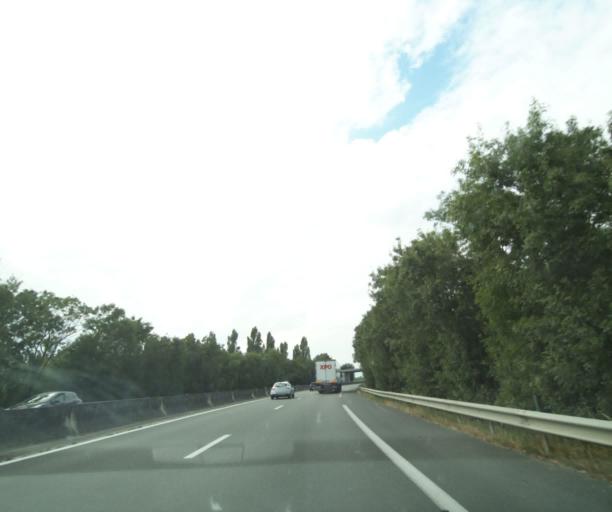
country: FR
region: Poitou-Charentes
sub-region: Departement de la Charente-Maritime
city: Aytre
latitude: 46.1218
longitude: -1.1097
